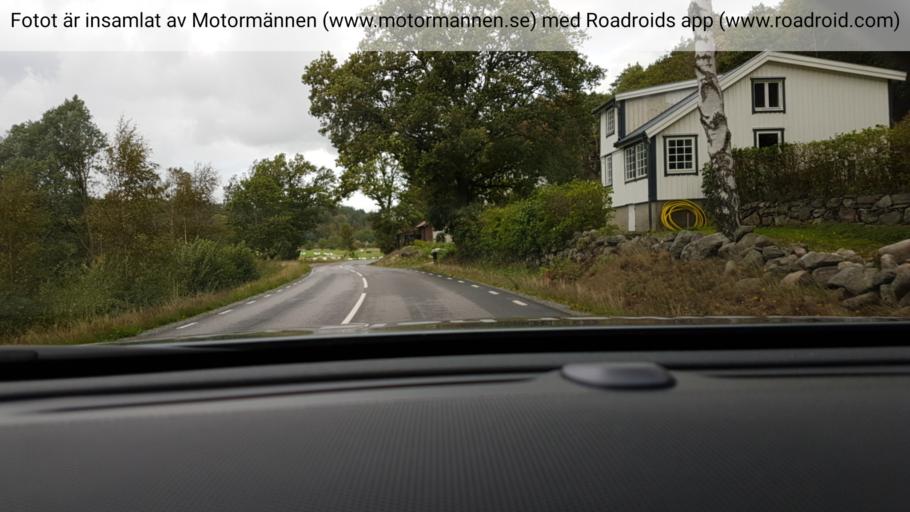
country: SE
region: Vaestra Goetaland
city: Svanesund
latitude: 58.1100
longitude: 11.8513
